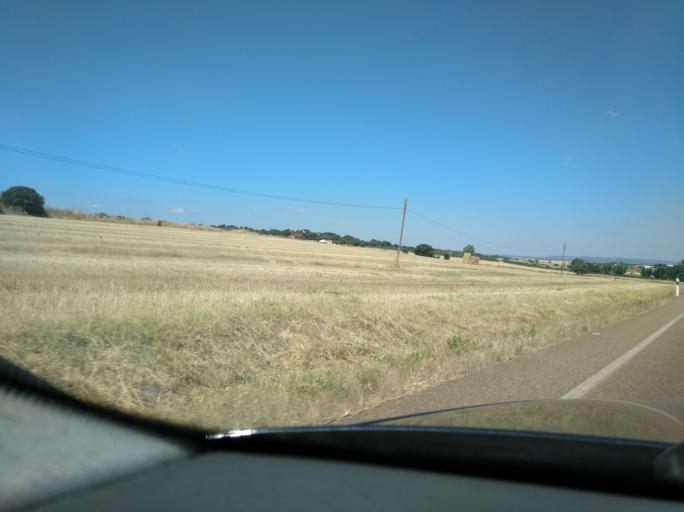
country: ES
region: Extremadura
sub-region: Provincia de Badajoz
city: Olivenza
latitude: 38.6978
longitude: -7.1047
